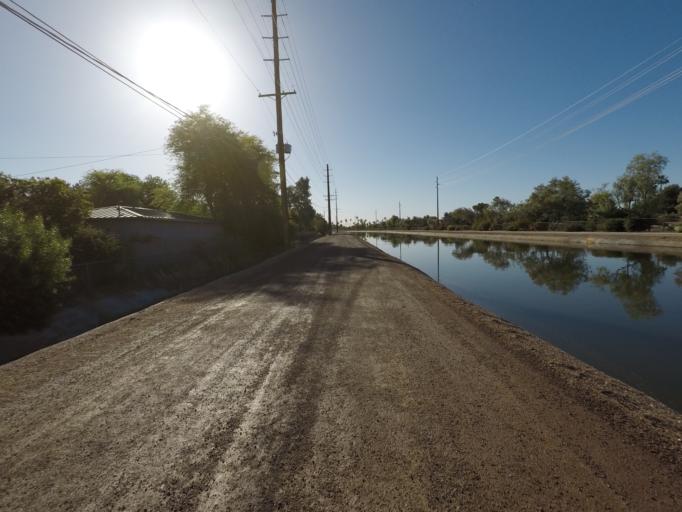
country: US
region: Arizona
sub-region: Maricopa County
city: Paradise Valley
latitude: 33.4909
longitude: -111.9518
